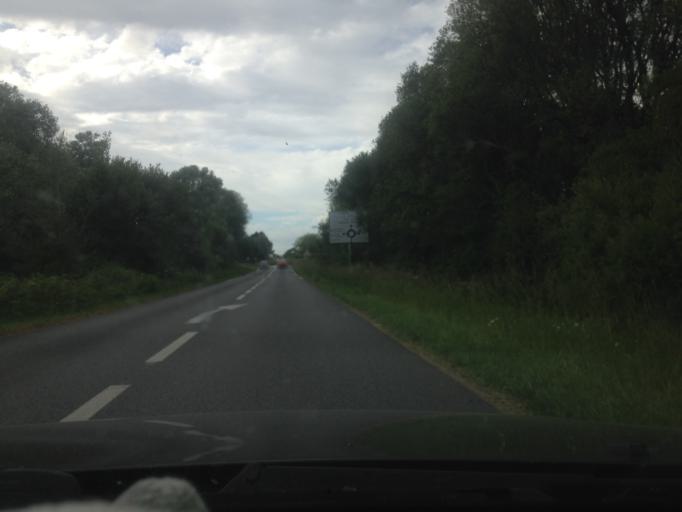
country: FR
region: Brittany
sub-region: Departement du Morbihan
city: Plouharnel
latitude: 47.6120
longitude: -3.1268
